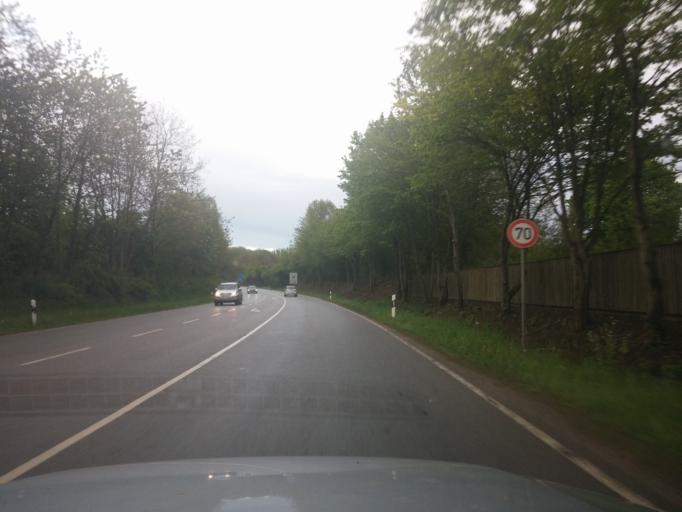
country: DE
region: Bavaria
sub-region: Upper Bavaria
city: Oberhaching
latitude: 48.0329
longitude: 11.5998
